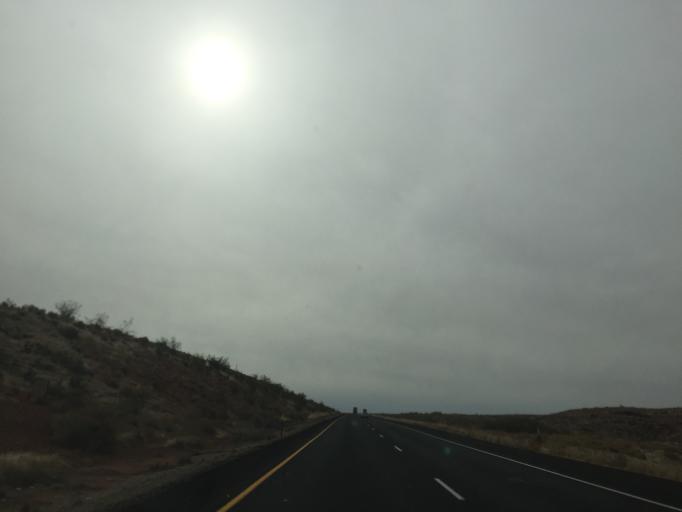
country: US
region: Utah
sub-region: Washington County
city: Washington
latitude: 37.1902
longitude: -113.4090
